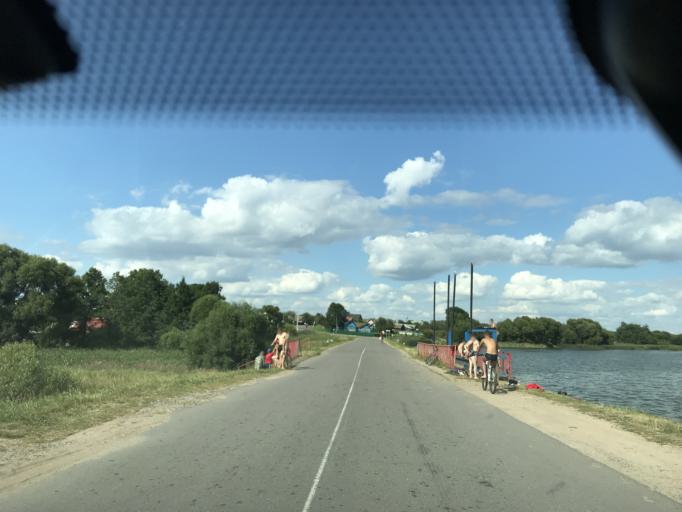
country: BY
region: Mogilev
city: Poselok Voskhod
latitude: 53.7797
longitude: 30.3485
